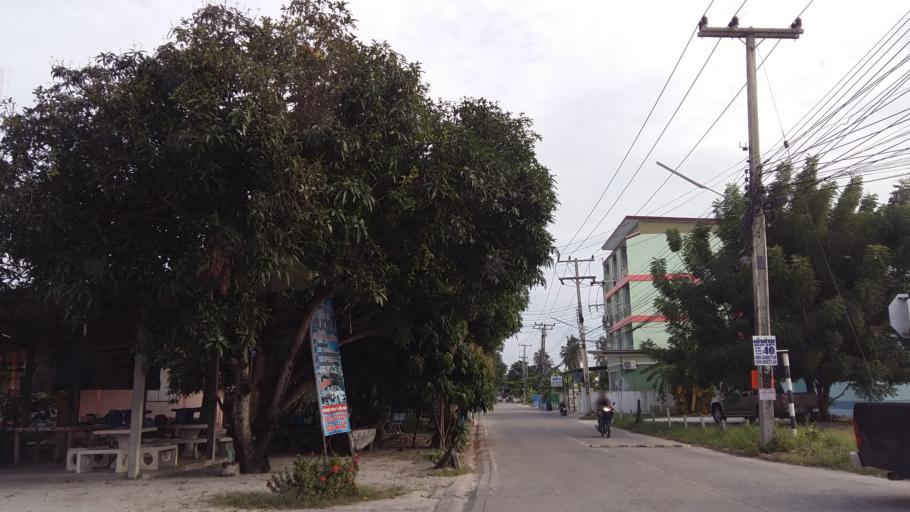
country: TH
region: Chon Buri
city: Chon Buri
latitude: 13.3094
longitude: 100.9379
